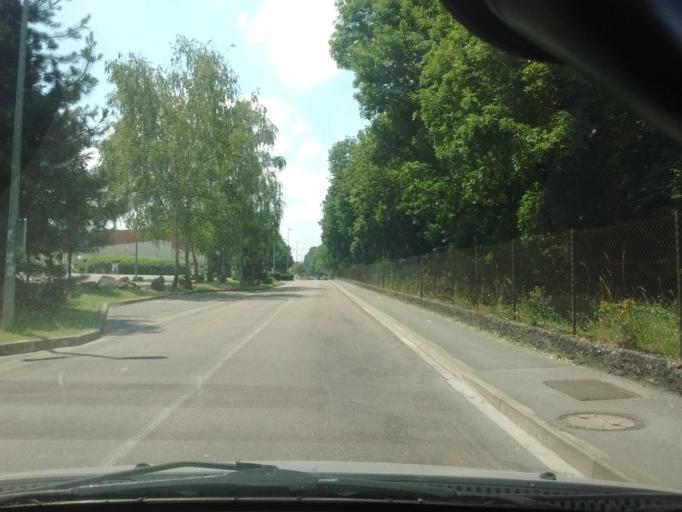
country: FR
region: Ile-de-France
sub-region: Departement de Seine-et-Marne
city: Ponthierry
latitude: 48.5268
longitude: 2.5440
